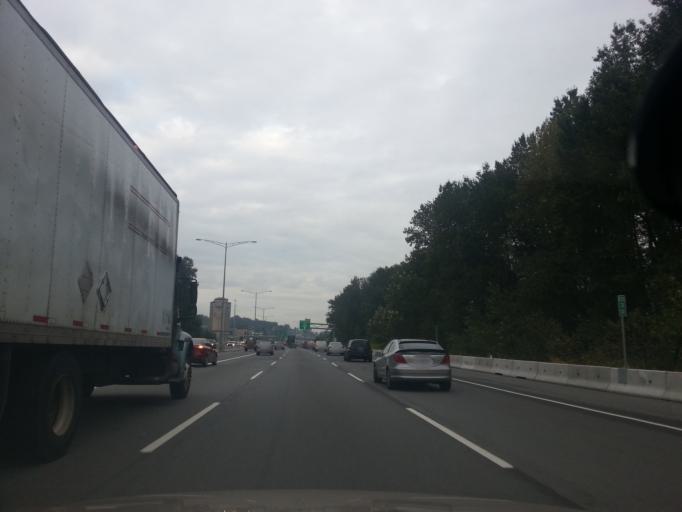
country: CA
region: British Columbia
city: Burnaby
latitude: 49.2580
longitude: -122.9938
